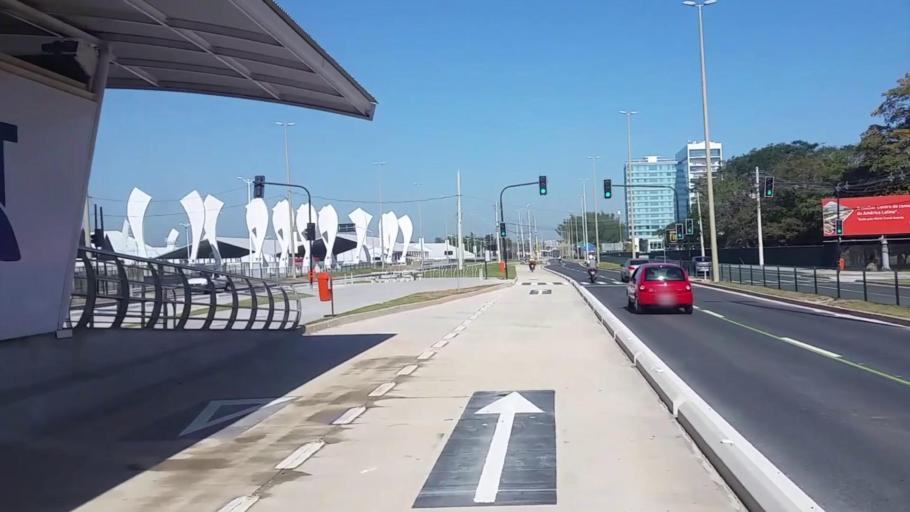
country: BR
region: Rio de Janeiro
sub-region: Nilopolis
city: Nilopolis
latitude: -22.9770
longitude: -43.4066
